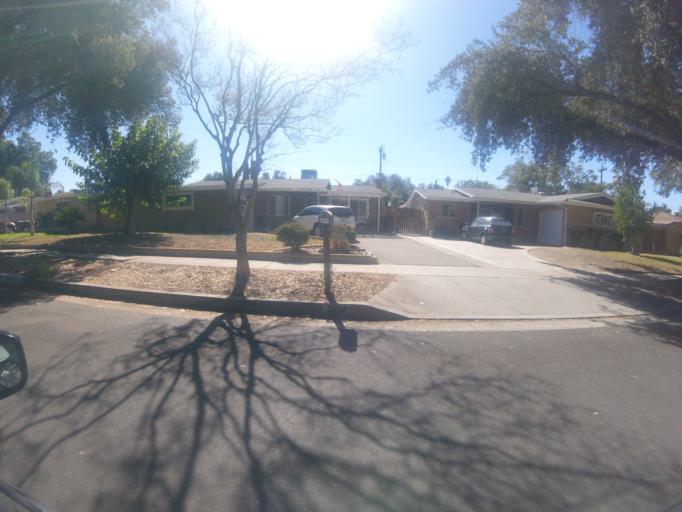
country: US
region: California
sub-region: San Bernardino County
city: Redlands
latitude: 34.0795
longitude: -117.1784
